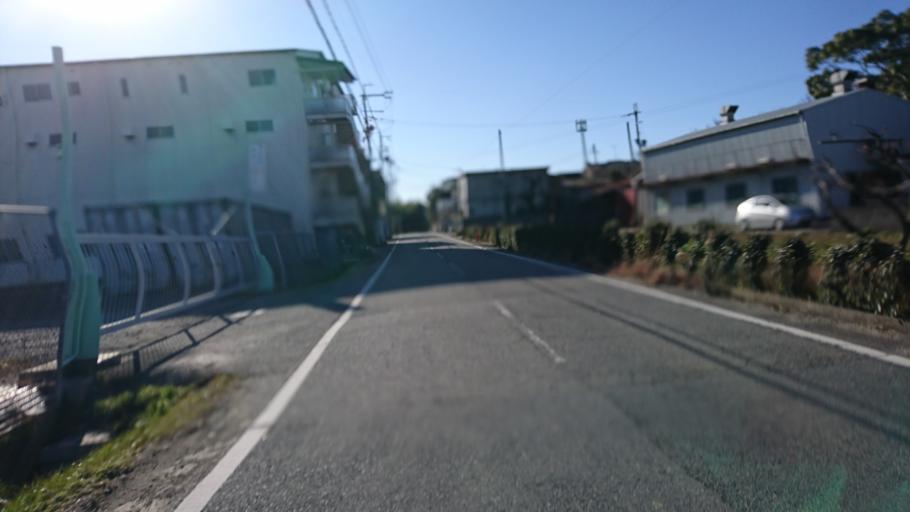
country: JP
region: Hyogo
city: Miki
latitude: 34.7554
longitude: 134.9258
